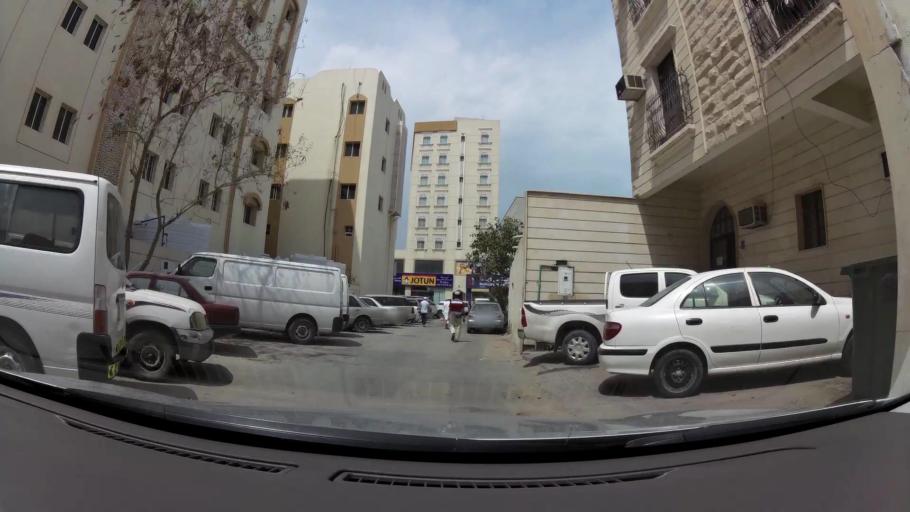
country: QA
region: Baladiyat ad Dawhah
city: Doha
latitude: 25.2761
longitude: 51.5227
